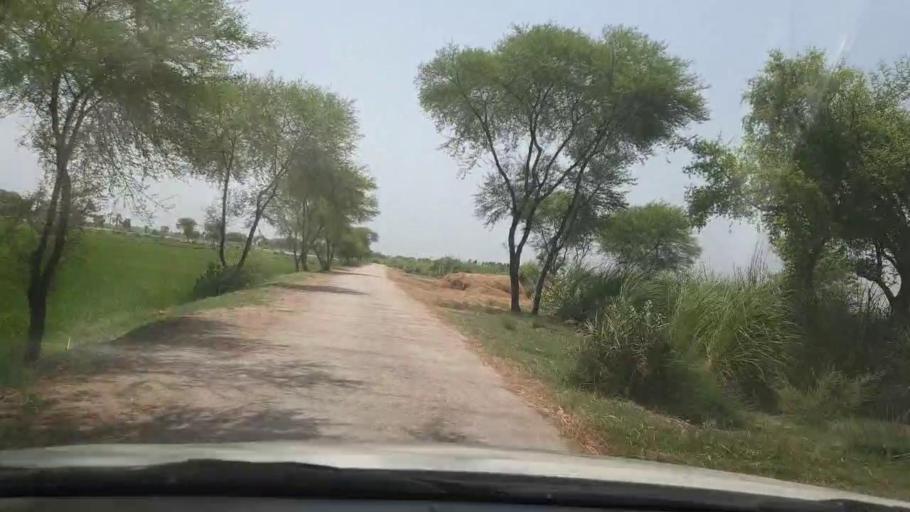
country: PK
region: Sindh
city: Shikarpur
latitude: 28.0722
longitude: 68.5388
